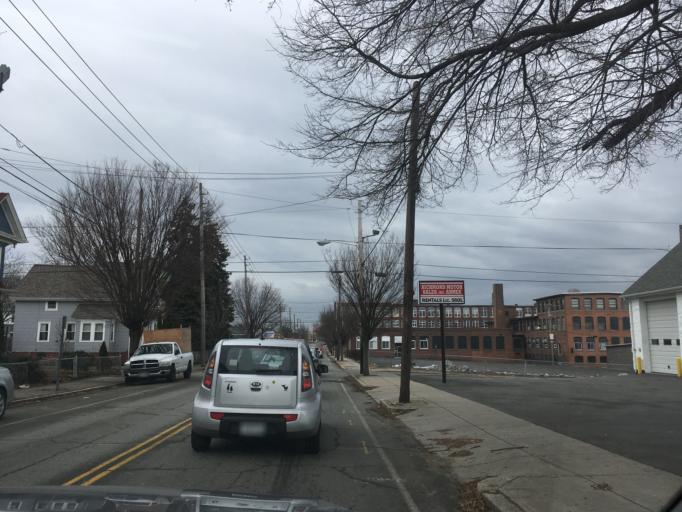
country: US
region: Rhode Island
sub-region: Providence County
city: Pawtucket
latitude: 41.8607
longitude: -71.3965
